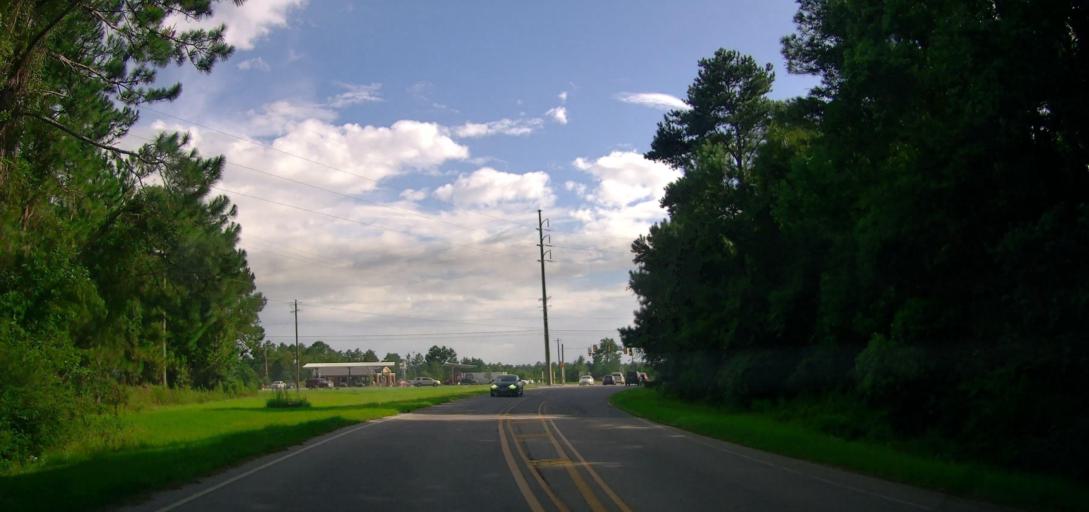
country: US
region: Georgia
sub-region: Coffee County
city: Douglas
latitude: 31.4892
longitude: -82.8590
